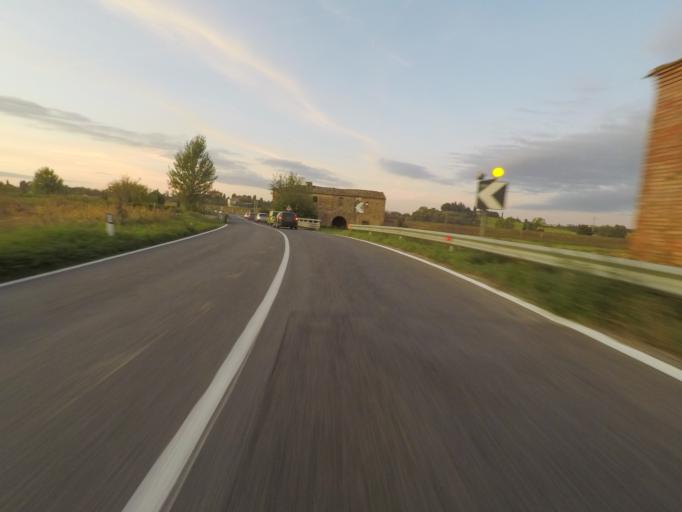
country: IT
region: Tuscany
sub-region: Provincia di Siena
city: Guazzino
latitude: 43.2035
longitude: 11.7659
